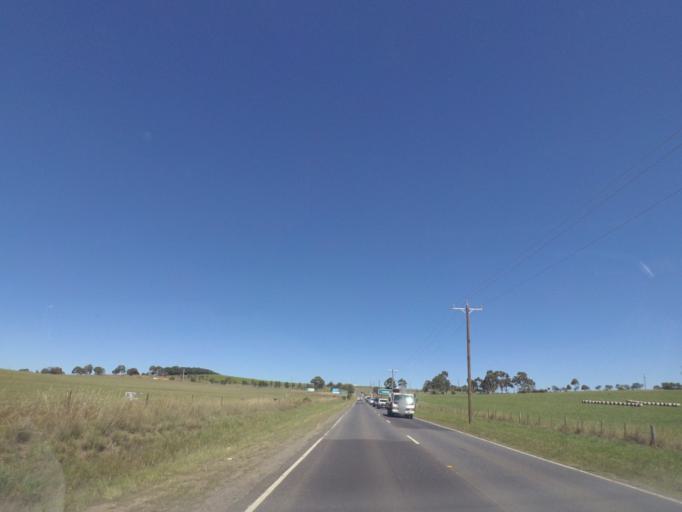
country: AU
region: Victoria
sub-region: Hume
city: Craigieburn
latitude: -37.5339
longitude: 144.8891
